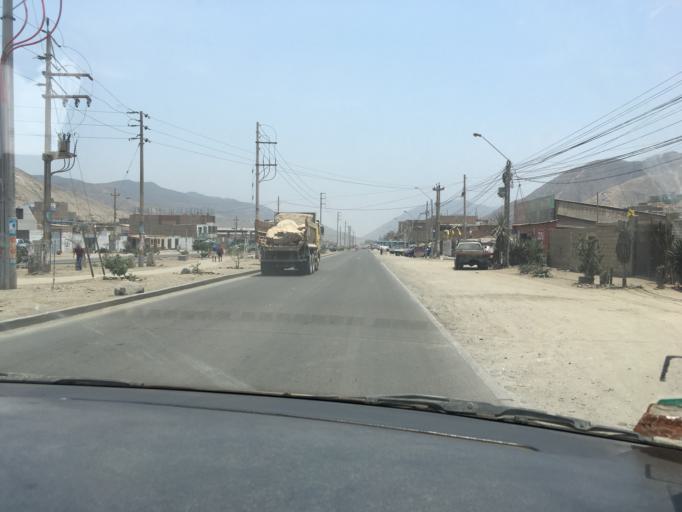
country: PE
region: Lima
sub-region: Lima
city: Cieneguilla
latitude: -12.1173
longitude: -76.8732
